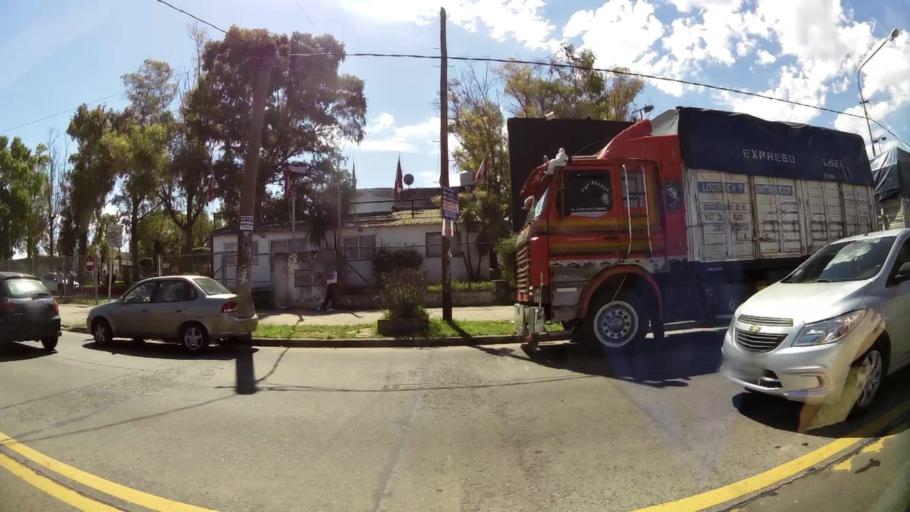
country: AR
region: Buenos Aires
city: San Justo
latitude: -34.6708
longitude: -58.5586
